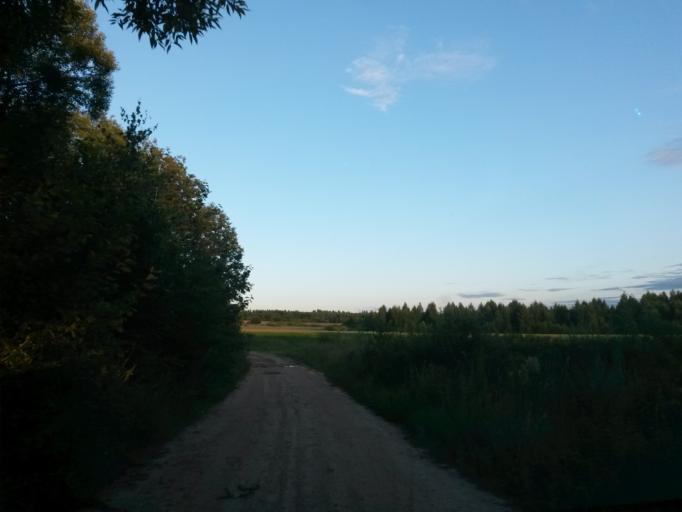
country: RU
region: Jaroslavl
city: Gavrilov-Yam
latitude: 57.3367
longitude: 40.0394
